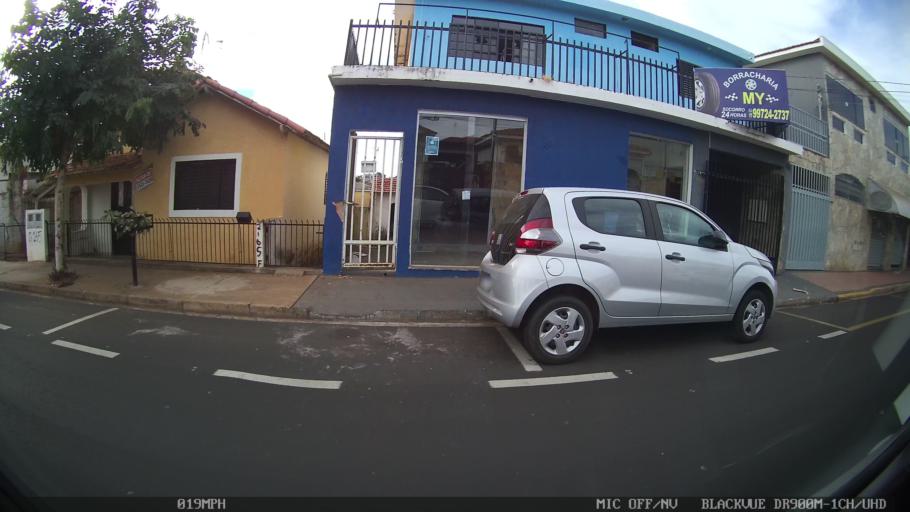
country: BR
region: Sao Paulo
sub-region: Catanduva
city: Catanduva
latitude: -21.1486
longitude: -48.9782
